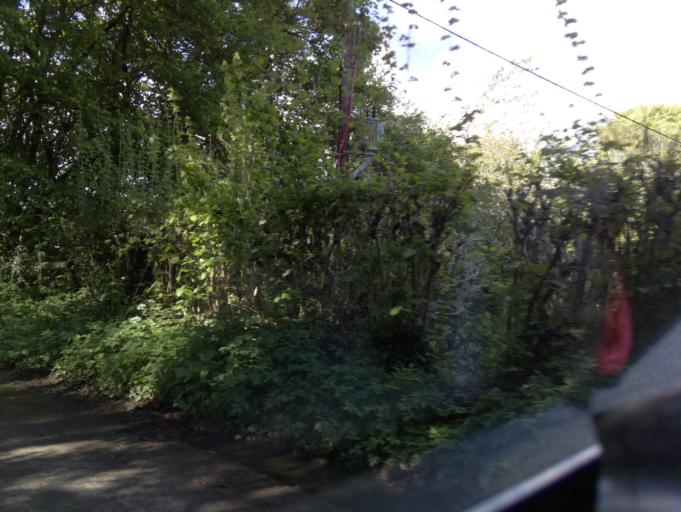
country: GB
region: Wales
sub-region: Caerphilly County Borough
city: Risca
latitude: 51.5755
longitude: -3.1082
